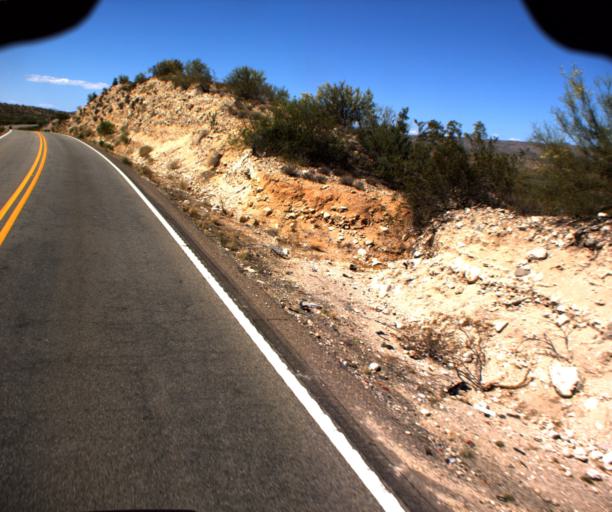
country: US
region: Arizona
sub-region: Yavapai County
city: Bagdad
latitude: 34.7950
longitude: -113.6232
